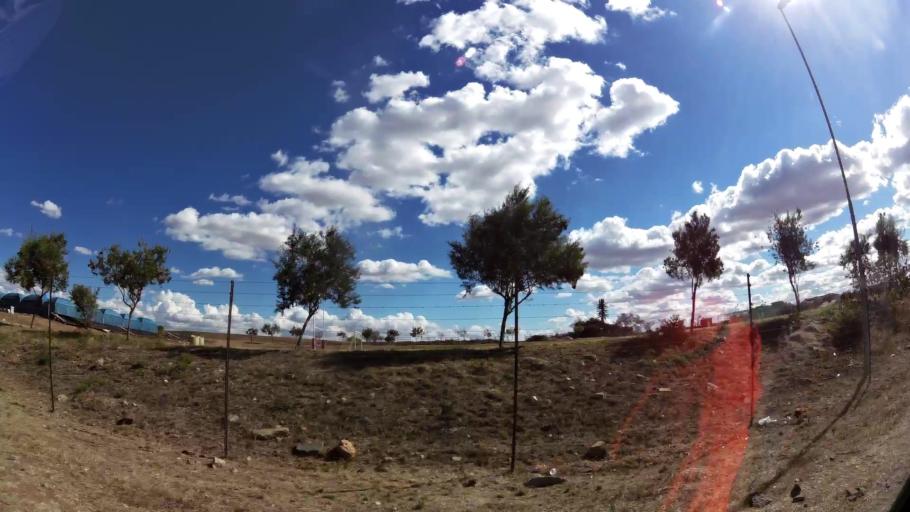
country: ZA
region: Limpopo
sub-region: Capricorn District Municipality
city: Polokwane
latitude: -23.8653
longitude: 29.5096
